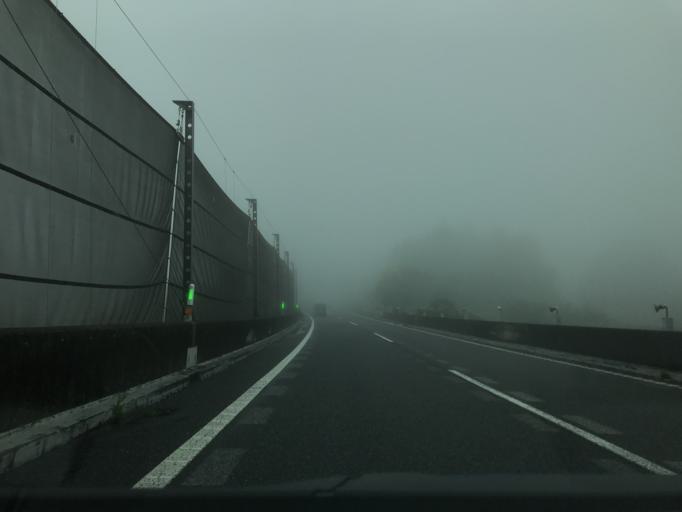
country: JP
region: Oita
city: Hiji
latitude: 33.3542
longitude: 131.4467
